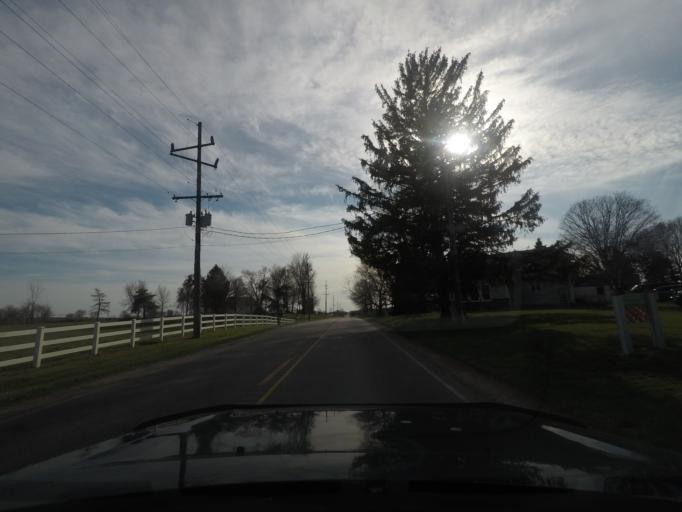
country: US
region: Indiana
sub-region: Elkhart County
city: Wakarusa
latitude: 41.5428
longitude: -85.9280
